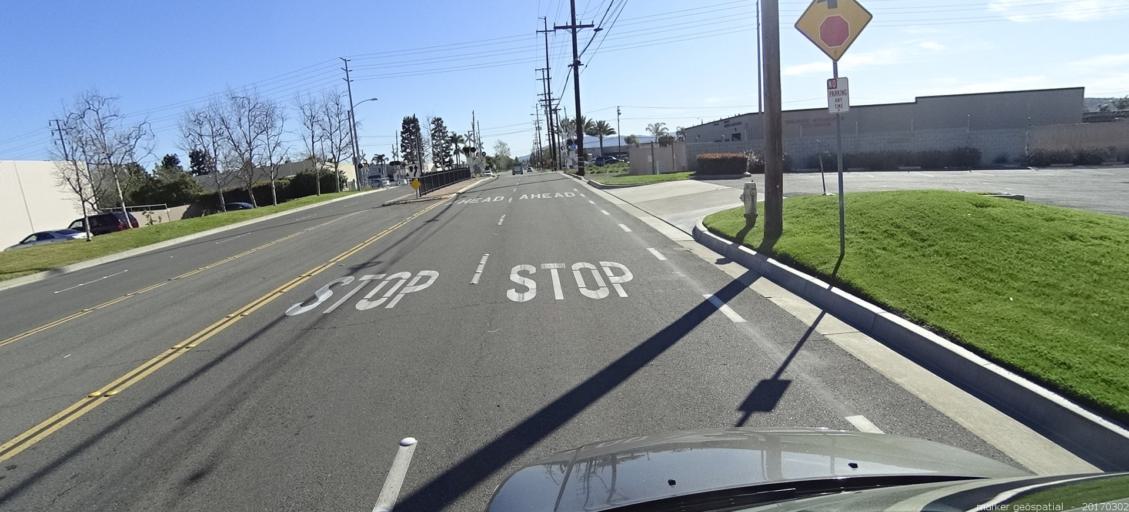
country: US
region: California
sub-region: Orange County
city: Placentia
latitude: 33.8627
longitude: -117.8386
